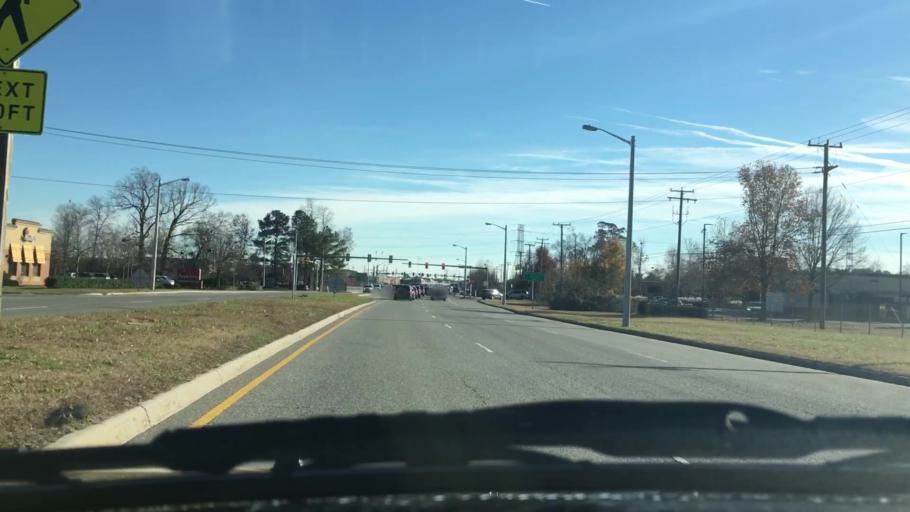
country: US
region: Virginia
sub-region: City of Portsmouth
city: Portsmouth Heights
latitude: 36.8829
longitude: -76.4265
